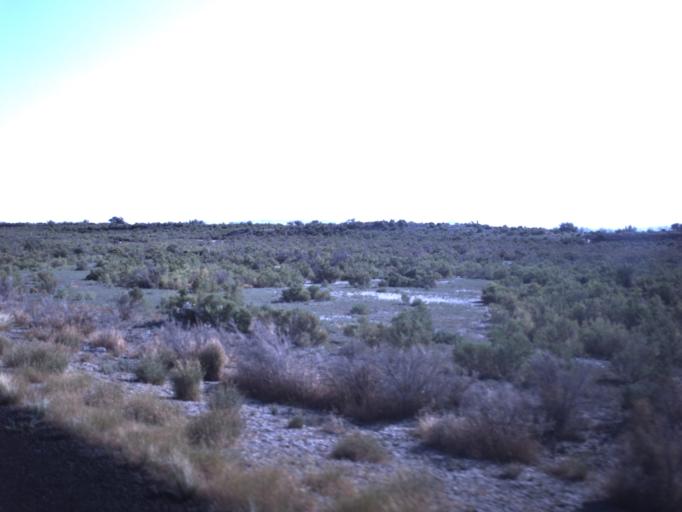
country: US
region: Utah
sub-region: Beaver County
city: Milford
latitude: 38.5916
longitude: -112.9881
